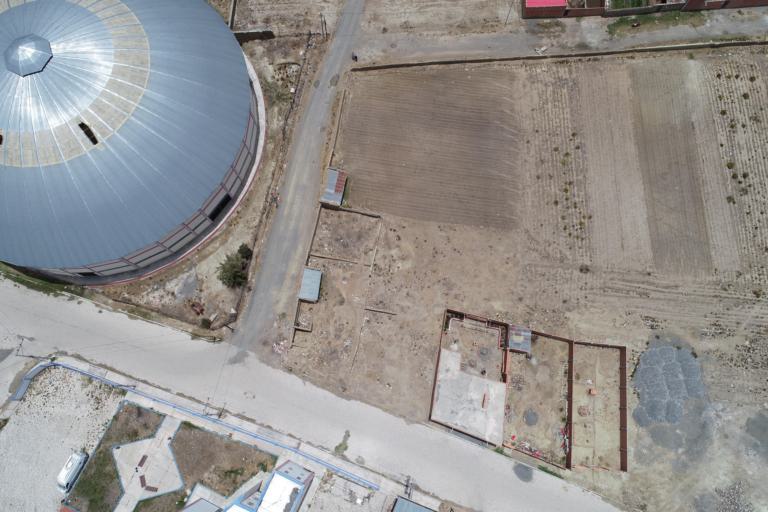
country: BO
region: La Paz
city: Achacachi
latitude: -16.0433
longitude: -68.6928
